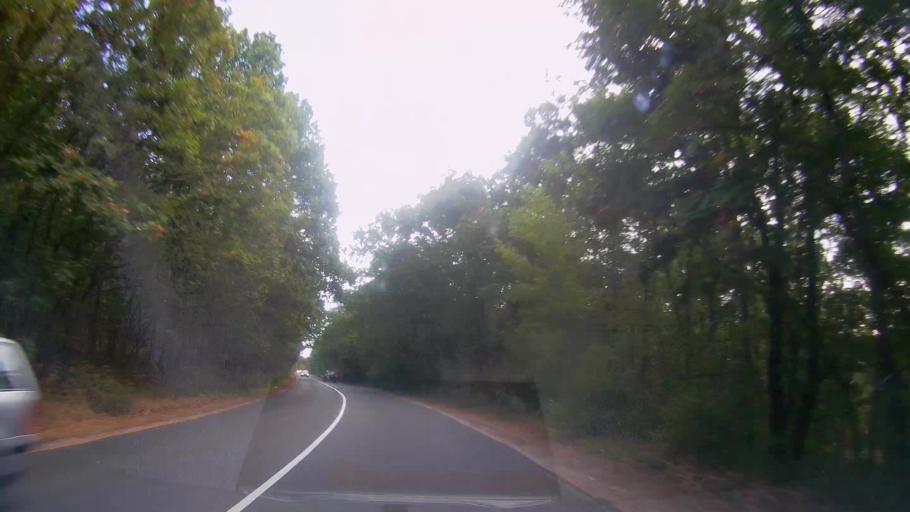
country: BG
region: Burgas
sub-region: Obshtina Primorsko
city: Primorsko
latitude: 42.2934
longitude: 27.7304
